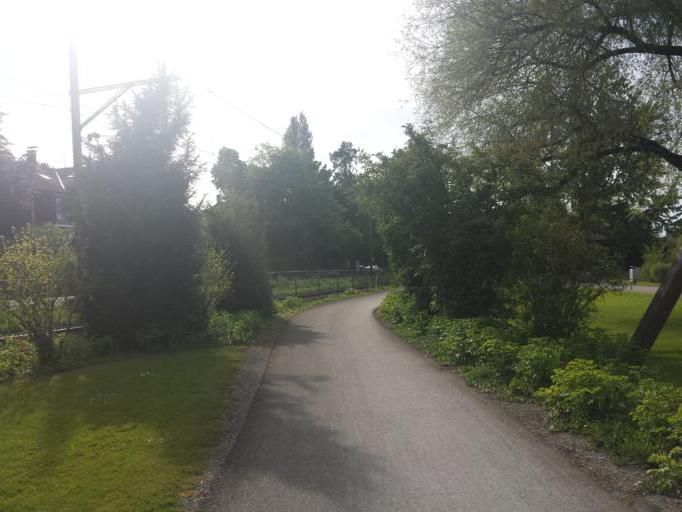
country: CH
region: Saint Gallen
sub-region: Wahlkreis Rorschach
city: Rorschach
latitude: 47.4808
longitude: 9.4824
